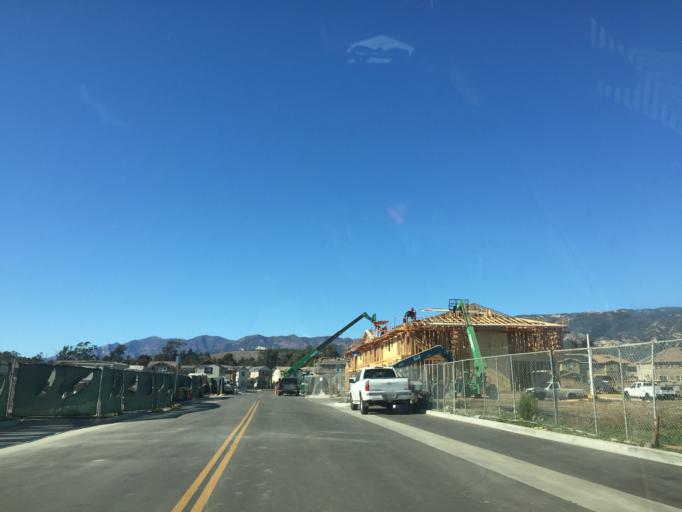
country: US
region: California
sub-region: Santa Barbara County
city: Isla Vista
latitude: 34.4332
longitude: -119.8586
